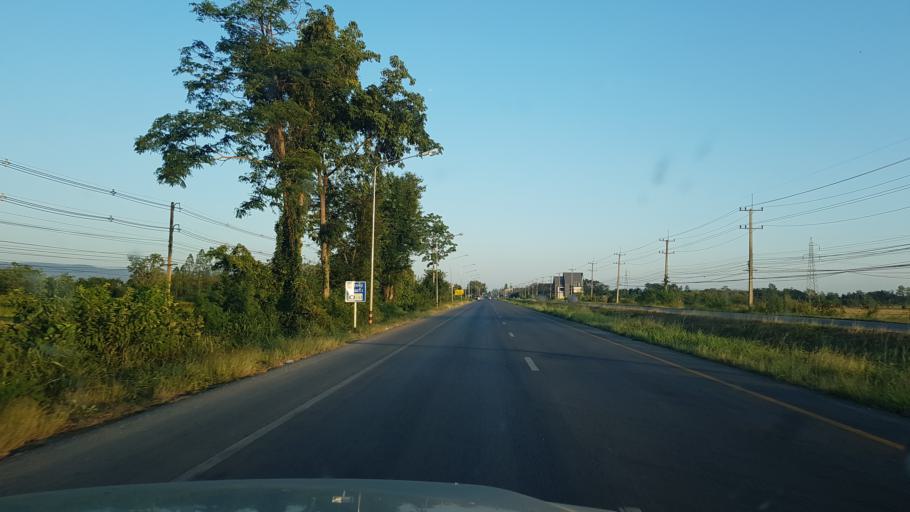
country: TH
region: Khon Kaen
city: Chum Phae
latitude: 16.5823
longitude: 102.0150
